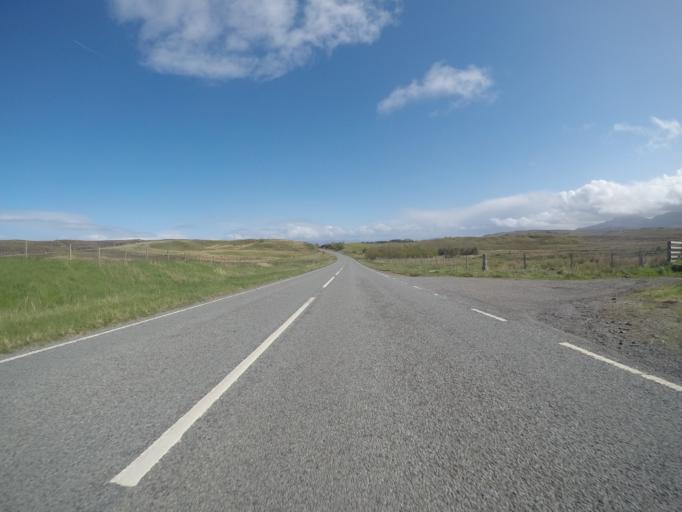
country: GB
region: Scotland
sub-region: Highland
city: Portree
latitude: 57.6166
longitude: -6.1902
